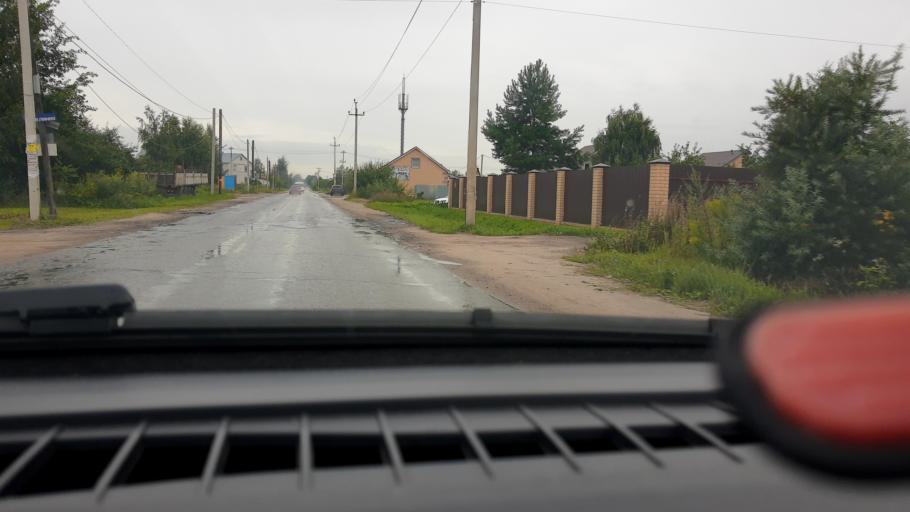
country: RU
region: Nizjnij Novgorod
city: Bor
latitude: 56.3530
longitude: 44.1162
